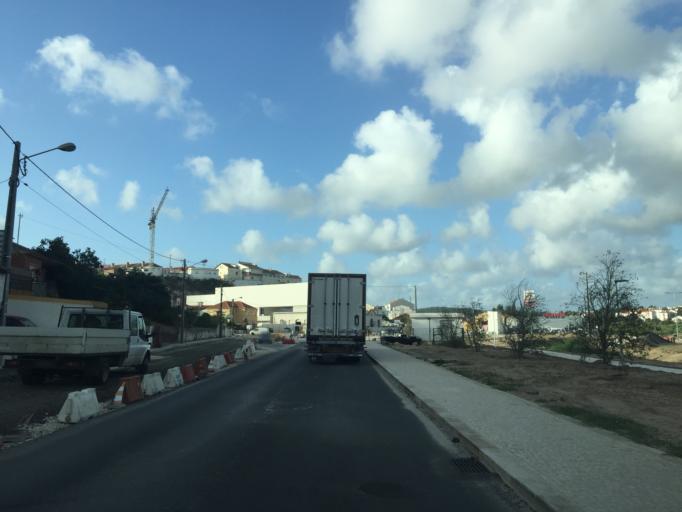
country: PT
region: Lisbon
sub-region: Torres Vedras
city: Torres Vedras
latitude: 39.0991
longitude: -9.2603
